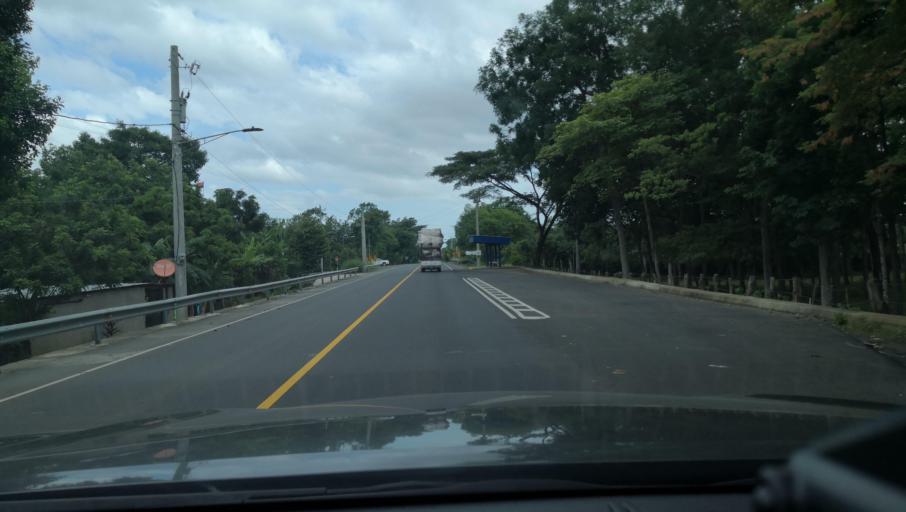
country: NI
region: Masaya
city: Nindiri
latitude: 12.0184
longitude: -86.1175
